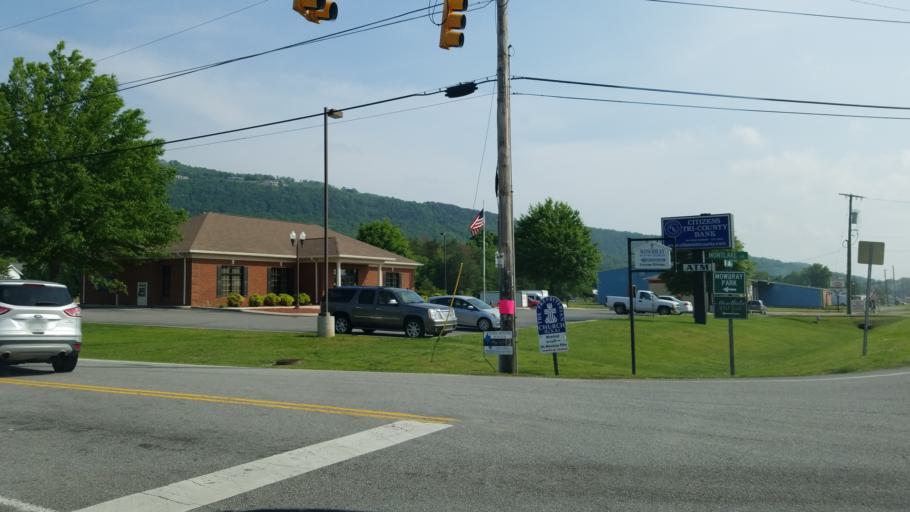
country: US
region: Tennessee
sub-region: Hamilton County
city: Soddy-Daisy
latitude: 35.2234
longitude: -85.2193
